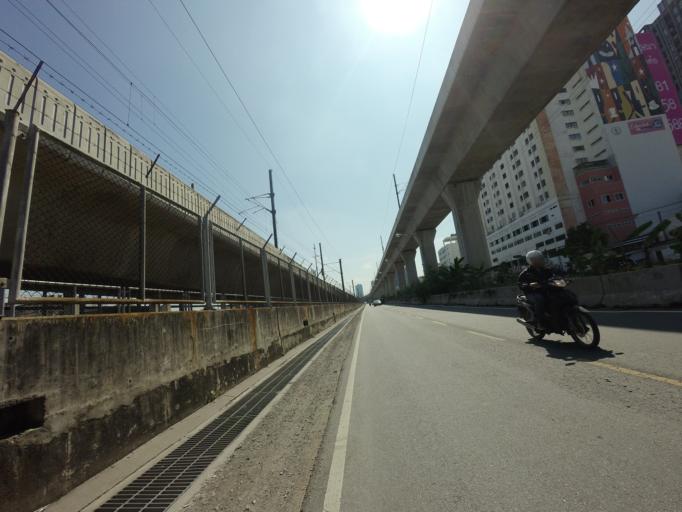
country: TH
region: Bangkok
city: Watthana
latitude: 13.7452
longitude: 100.5864
